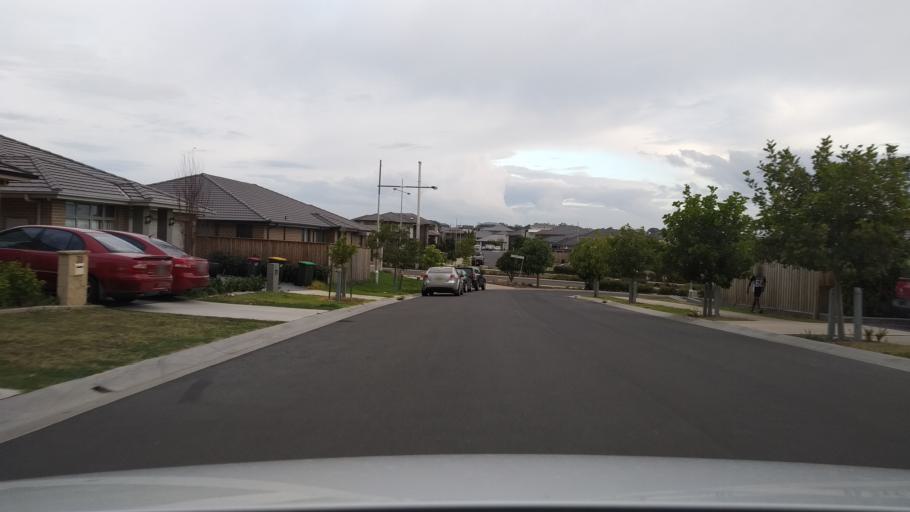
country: AU
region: New South Wales
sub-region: Camden
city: Narellan
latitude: -34.0044
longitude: 150.7282
